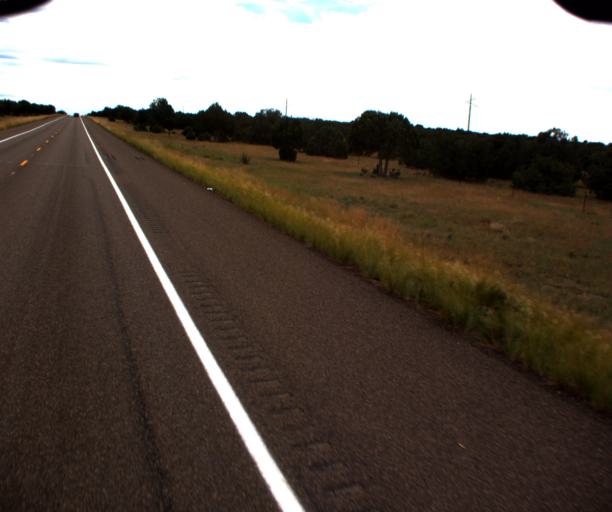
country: US
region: Arizona
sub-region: Navajo County
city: White Mountain Lake
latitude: 34.3153
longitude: -110.0409
